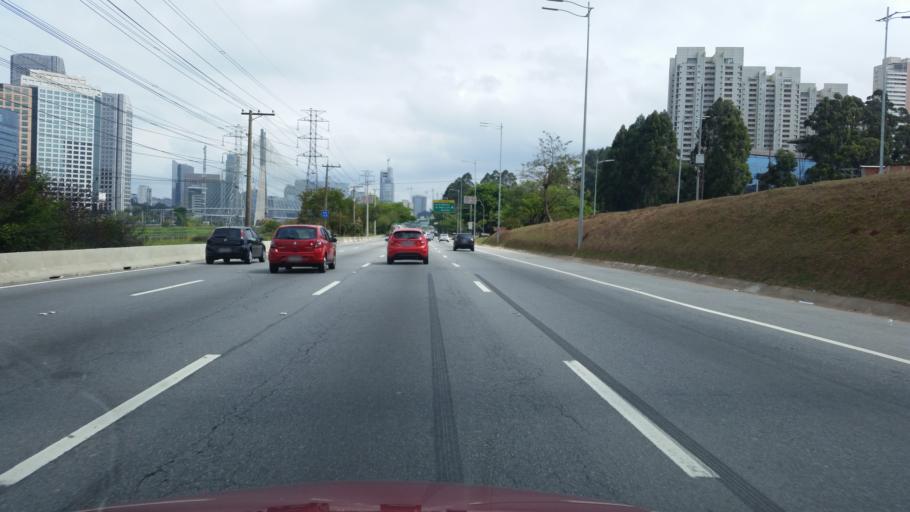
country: BR
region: Sao Paulo
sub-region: Sao Paulo
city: Sao Paulo
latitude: -23.6027
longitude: -46.6978
